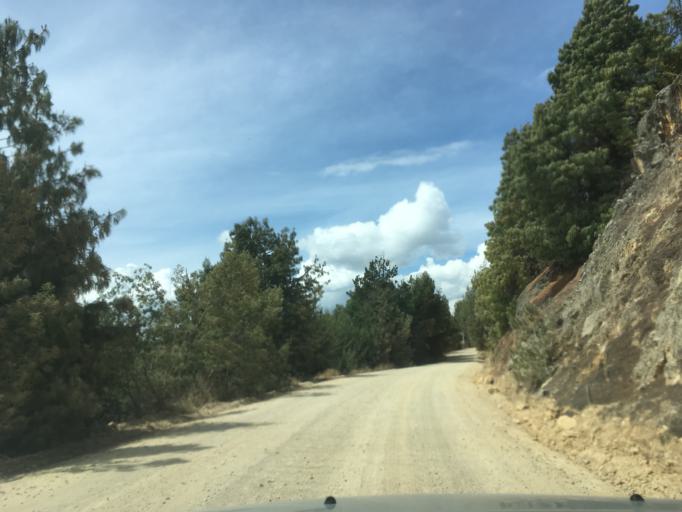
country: CO
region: Boyaca
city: Aquitania
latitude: 5.5742
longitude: -72.9395
